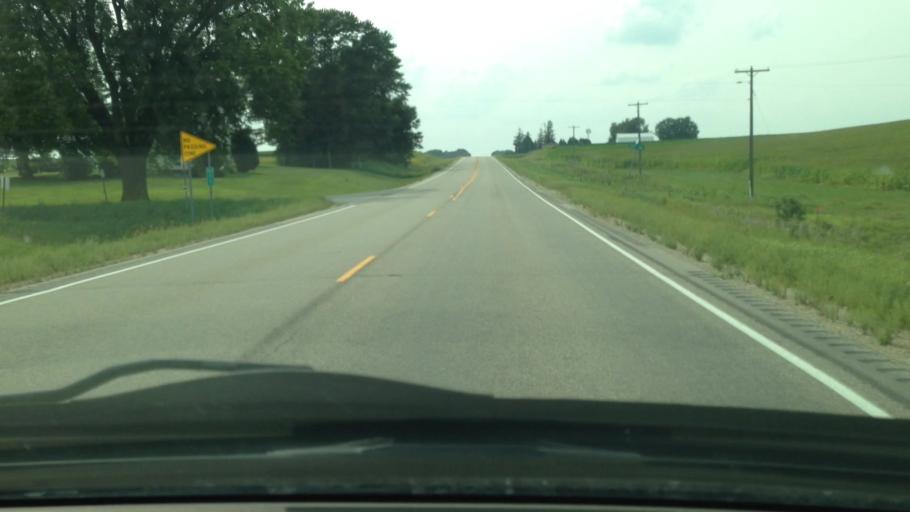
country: US
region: Minnesota
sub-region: Wabasha County
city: Plainview
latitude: 44.1652
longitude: -92.1988
